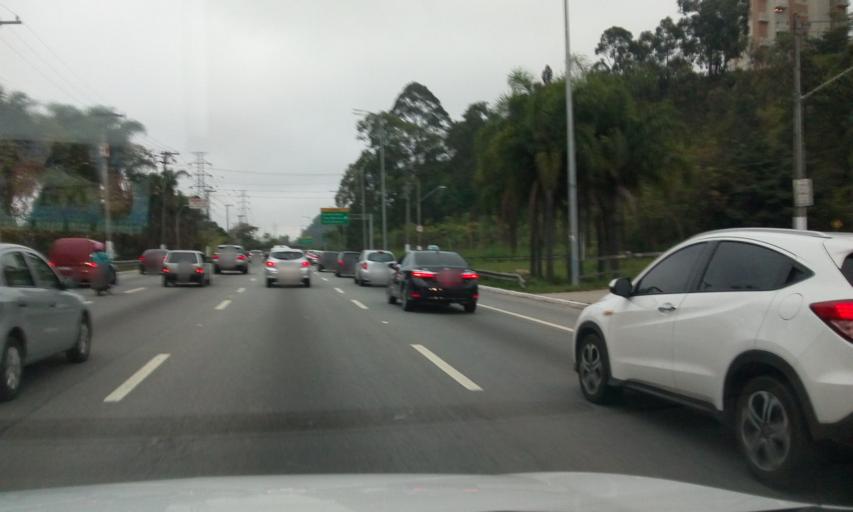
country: BR
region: Sao Paulo
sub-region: Taboao Da Serra
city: Taboao da Serra
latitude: -23.6304
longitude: -46.7169
